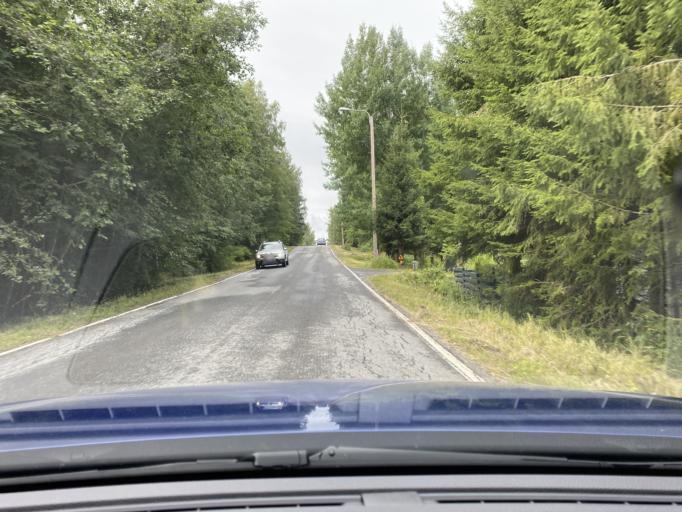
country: FI
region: Pirkanmaa
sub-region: Ylae-Pirkanmaa
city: Maenttae
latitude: 62.0267
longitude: 24.7133
